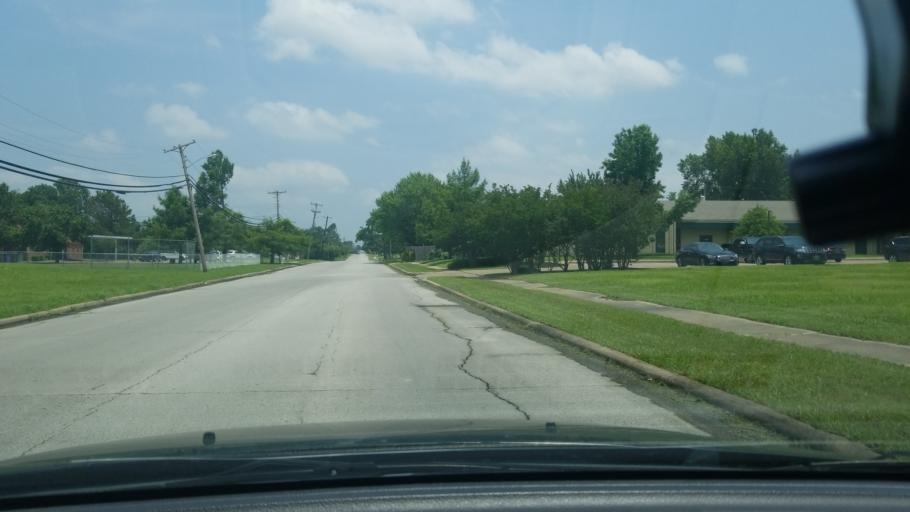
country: US
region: Texas
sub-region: Dallas County
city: Mesquite
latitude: 32.8002
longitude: -96.6465
